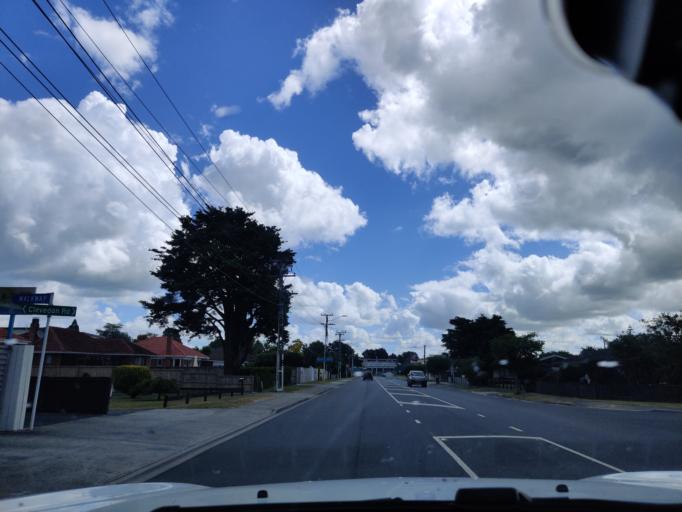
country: NZ
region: Auckland
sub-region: Auckland
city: Papakura
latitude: -37.0610
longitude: 174.9499
